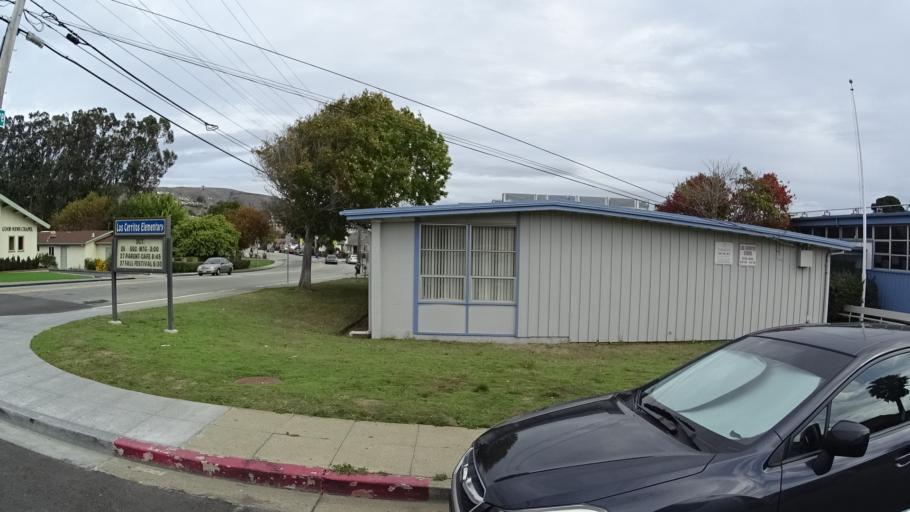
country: US
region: California
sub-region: San Mateo County
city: South San Francisco
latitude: 37.6512
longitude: -122.4280
